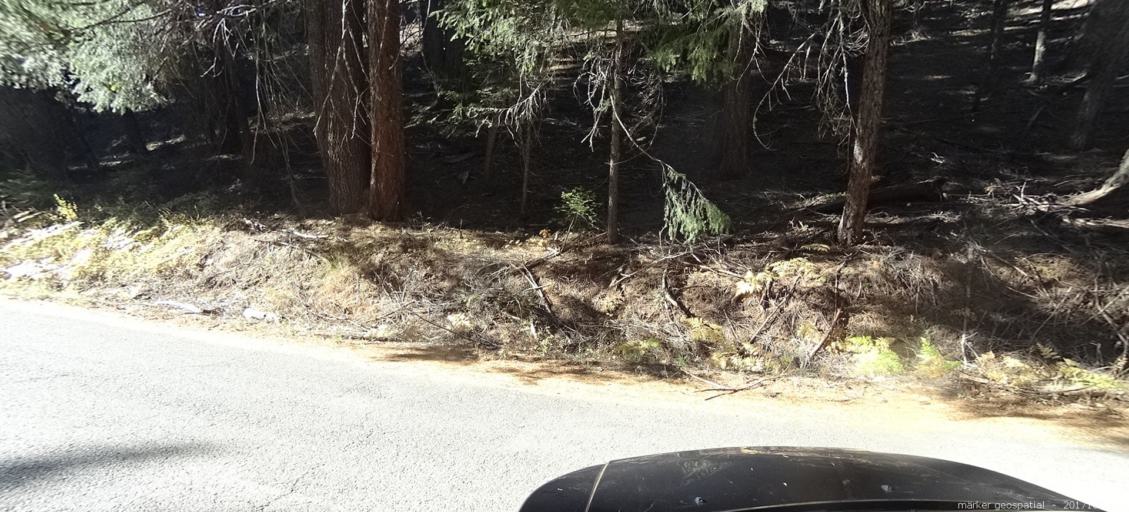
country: US
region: California
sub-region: Trinity County
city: Lewiston
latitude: 40.8232
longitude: -122.6632
